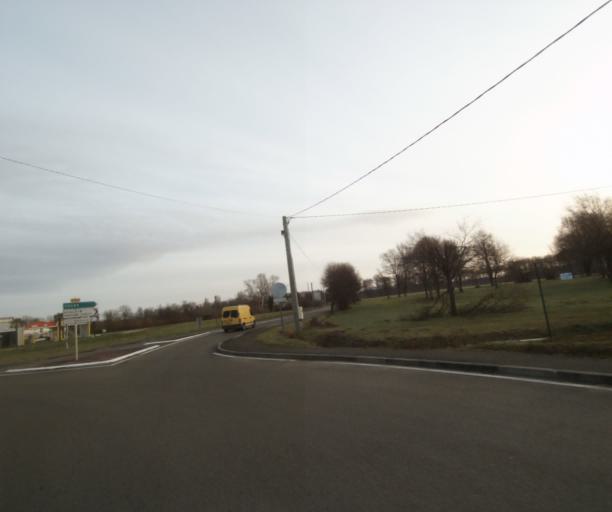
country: FR
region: Pays de la Loire
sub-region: Departement de la Sarthe
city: Arnage
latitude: 47.9364
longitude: 0.2155
